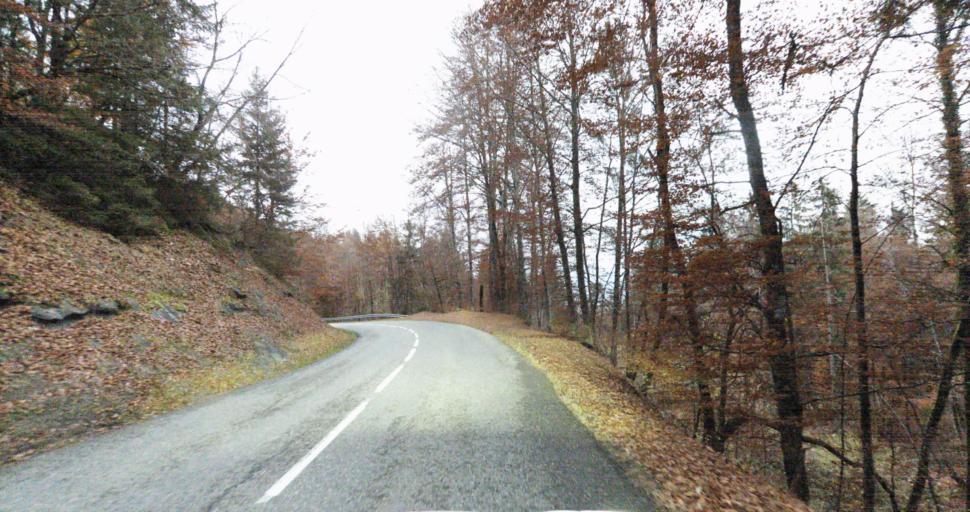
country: FR
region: Rhone-Alpes
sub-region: Departement de la Haute-Savoie
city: Saint-Jorioz
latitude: 45.8046
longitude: 6.1359
